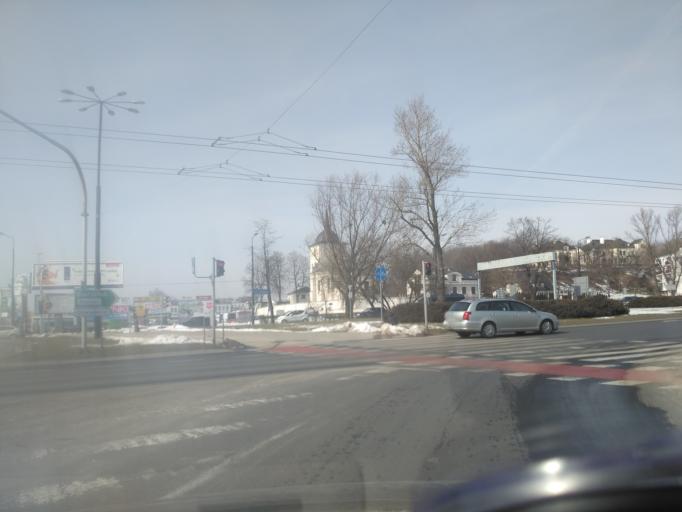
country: PL
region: Lublin Voivodeship
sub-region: Powiat lubelski
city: Lublin
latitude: 51.2514
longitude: 22.5759
